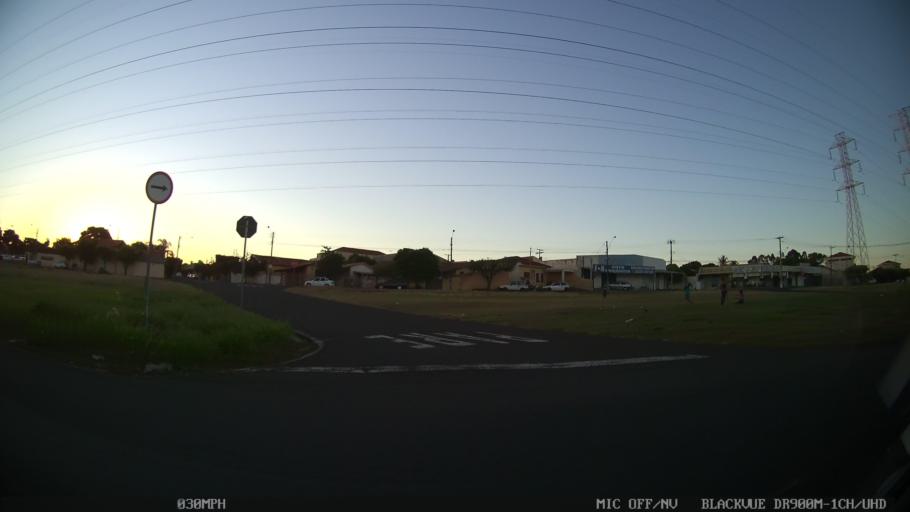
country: BR
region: Sao Paulo
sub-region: Sao Jose Do Rio Preto
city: Sao Jose do Rio Preto
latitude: -20.8435
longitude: -49.3769
